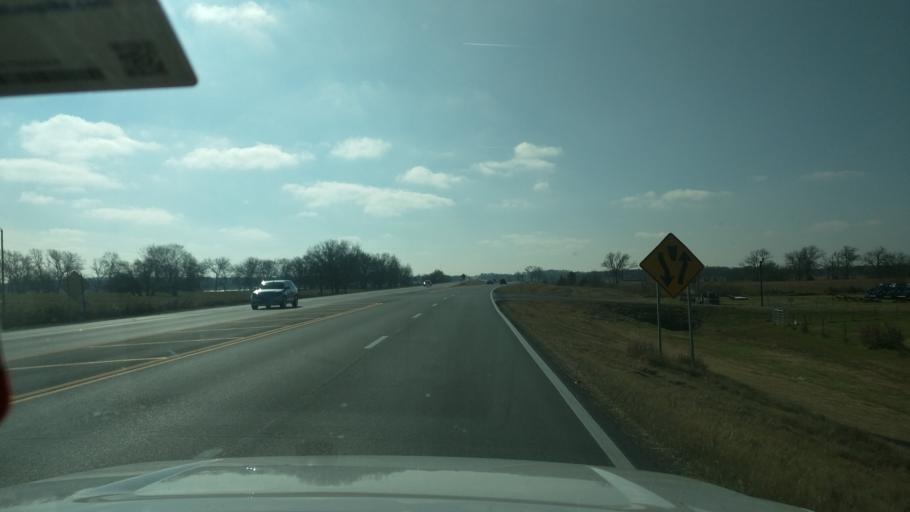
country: US
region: Oklahoma
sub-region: Washington County
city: Bartlesville
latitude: 36.6686
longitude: -95.9353
